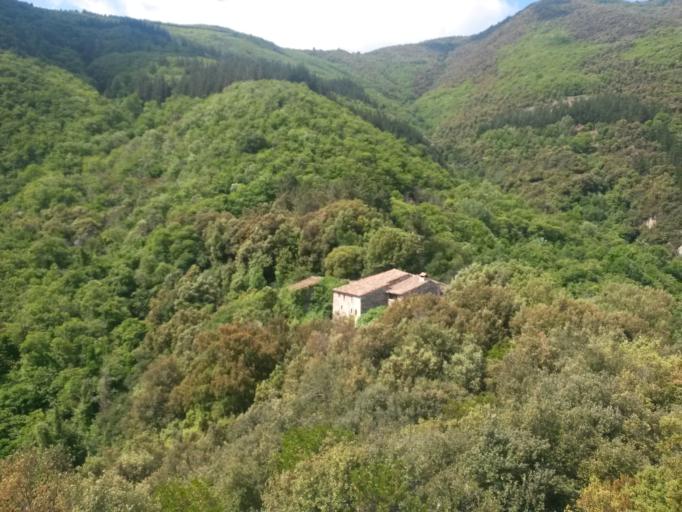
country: ES
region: Catalonia
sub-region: Provincia de Girona
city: la Cellera de Ter
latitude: 41.9708
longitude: 2.5882
